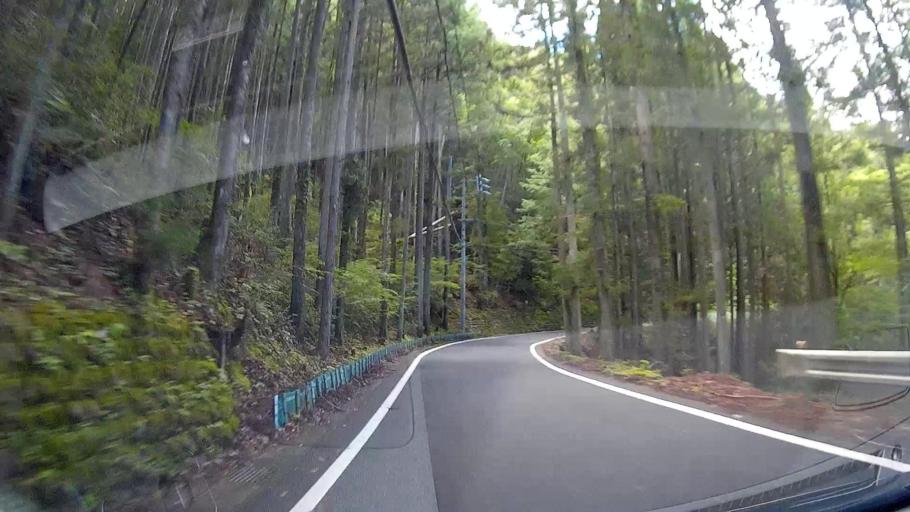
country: JP
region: Shizuoka
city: Shizuoka-shi
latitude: 35.2271
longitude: 138.2452
